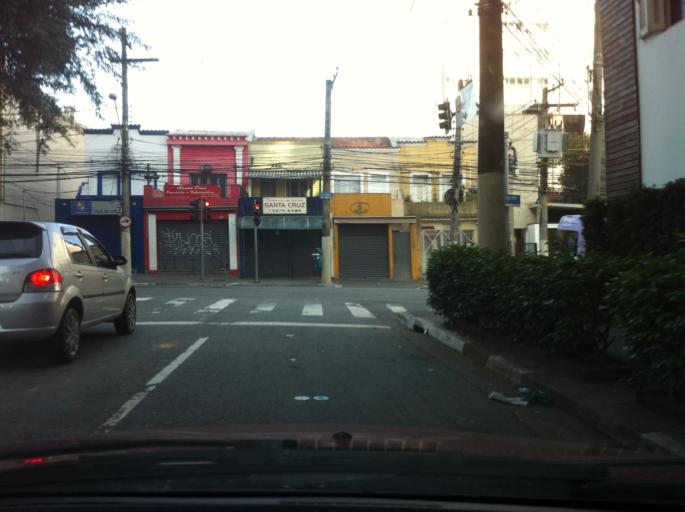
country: BR
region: Sao Paulo
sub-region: Sao Paulo
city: Sao Paulo
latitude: -23.5993
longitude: -46.6376
